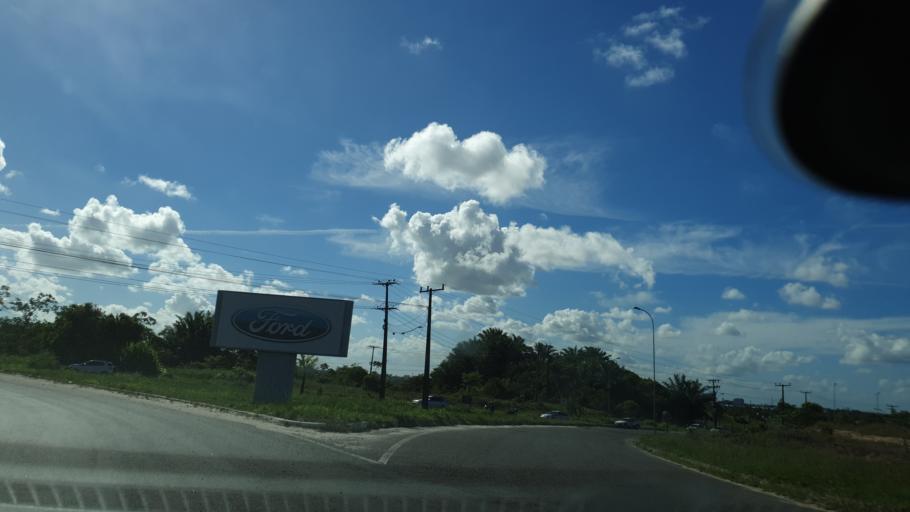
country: BR
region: Bahia
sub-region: Camacari
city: Camacari
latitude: -12.6791
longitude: -38.2825
